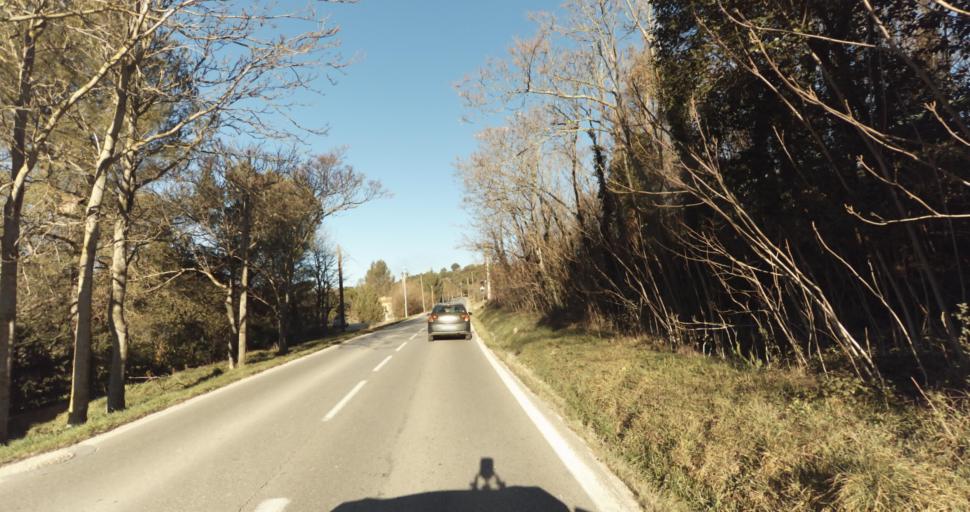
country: FR
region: Provence-Alpes-Cote d'Azur
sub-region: Departement des Bouches-du-Rhone
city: La Bouilladisse
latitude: 43.3935
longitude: 5.5884
